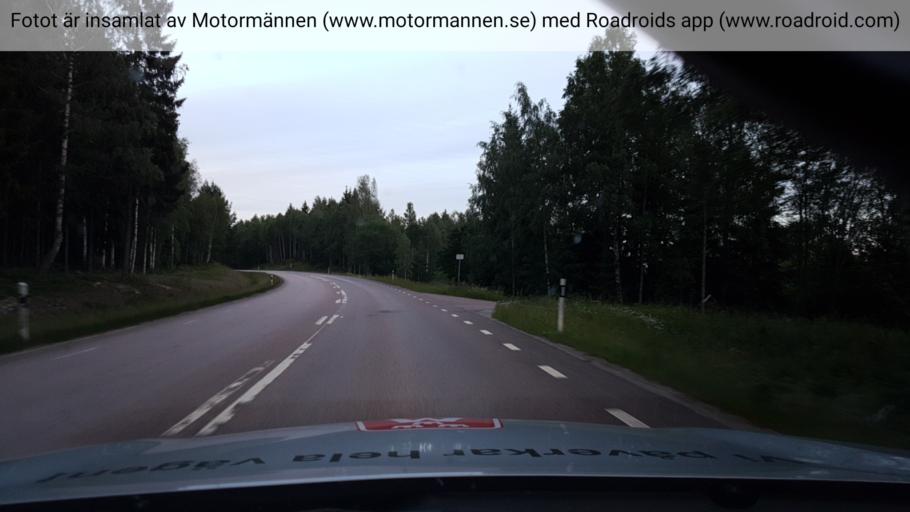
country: SE
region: Vaestmanland
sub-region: Skinnskattebergs Kommun
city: Skinnskatteberg
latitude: 59.9098
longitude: 15.7181
